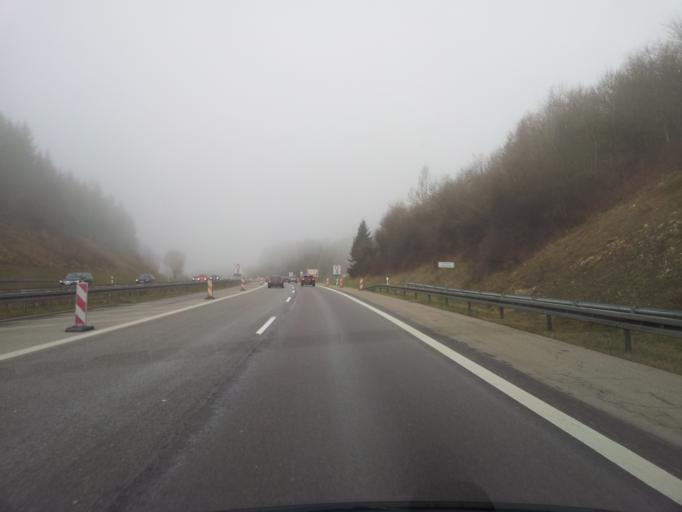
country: DE
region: Baden-Wuerttemberg
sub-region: Freiburg Region
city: Immendingen
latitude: 47.8916
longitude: 8.7256
